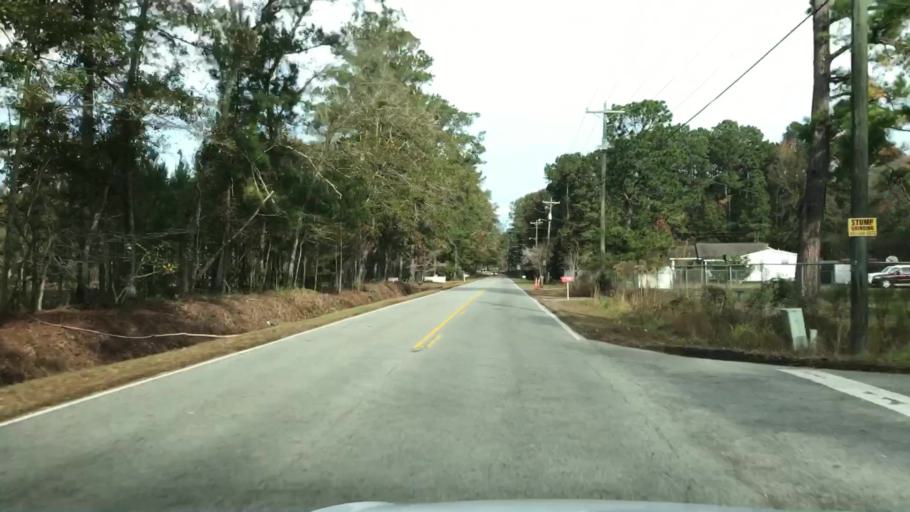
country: US
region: South Carolina
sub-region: Charleston County
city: Ravenel
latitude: 32.7704
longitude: -80.2431
